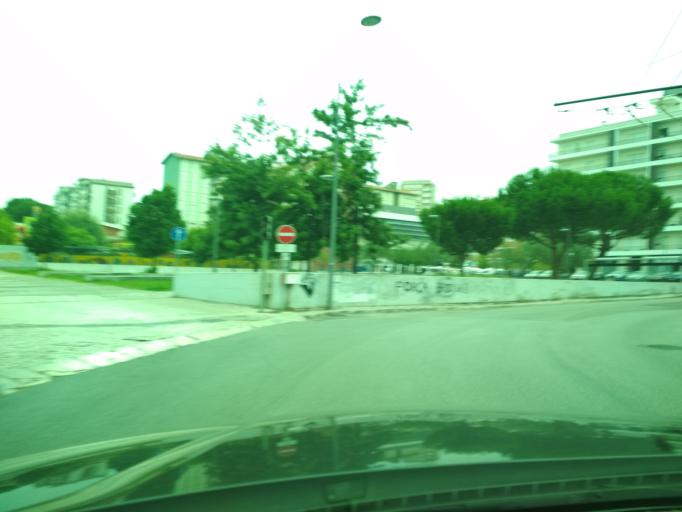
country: PT
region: Coimbra
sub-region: Coimbra
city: Coimbra
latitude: 40.2026
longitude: -8.4064
